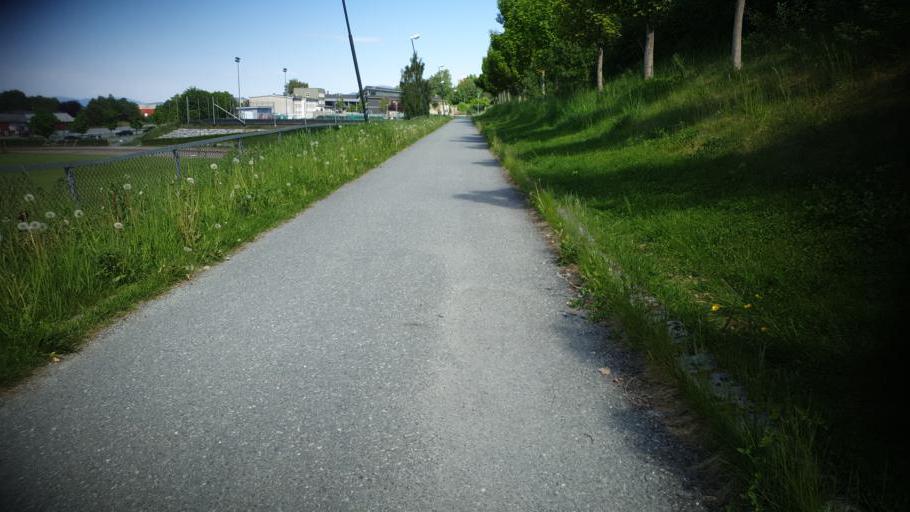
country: NO
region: Sor-Trondelag
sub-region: Malvik
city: Malvik
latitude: 63.4367
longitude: 10.6307
